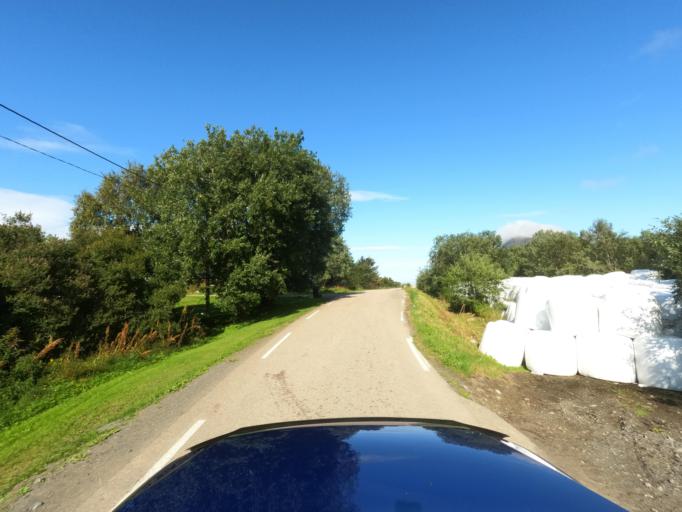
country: NO
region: Nordland
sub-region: Vestvagoy
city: Evjen
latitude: 68.3048
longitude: 14.0993
